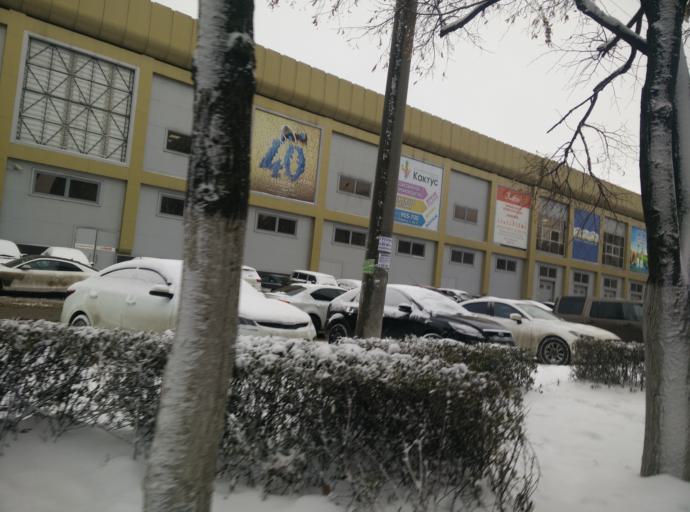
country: RU
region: Lipetsk
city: Lipetsk
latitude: 52.6068
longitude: 39.5787
